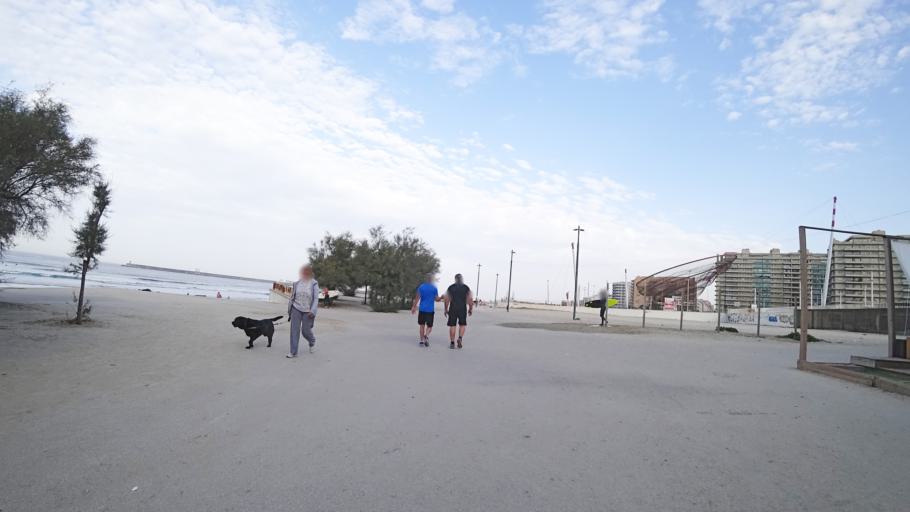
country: PT
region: Porto
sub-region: Matosinhos
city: Matosinhos
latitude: 41.1717
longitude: -8.6883
